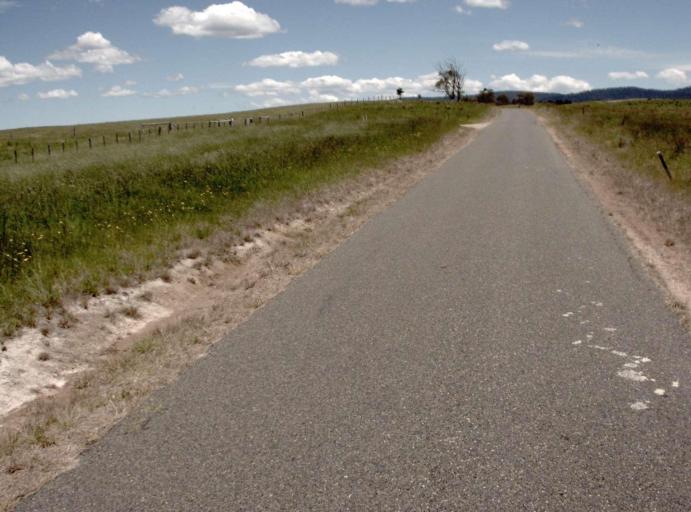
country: AU
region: New South Wales
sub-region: Snowy River
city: Jindabyne
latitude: -37.0880
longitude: 148.2707
